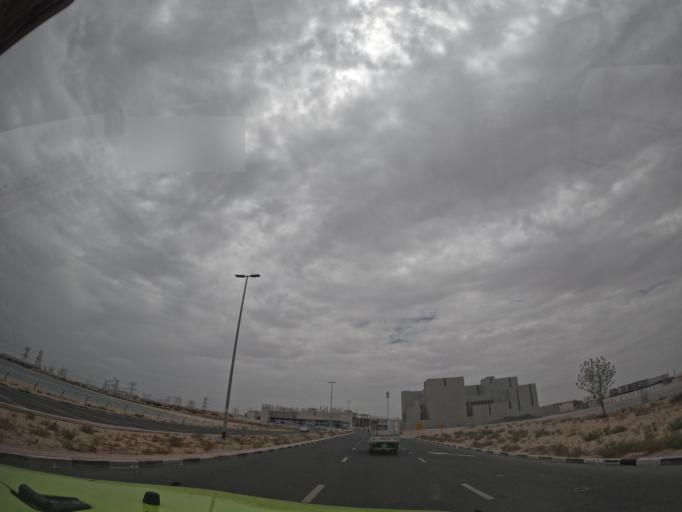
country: AE
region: Ash Shariqah
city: Sharjah
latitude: 25.1604
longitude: 55.3649
